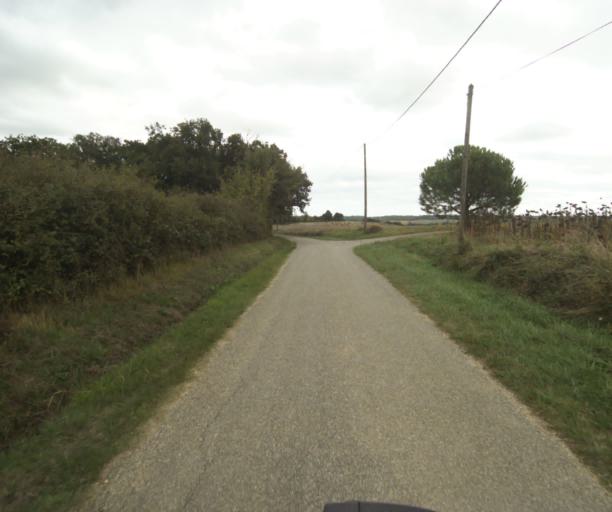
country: FR
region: Midi-Pyrenees
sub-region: Departement du Tarn-et-Garonne
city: Beaumont-de-Lomagne
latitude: 43.8559
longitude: 1.0626
